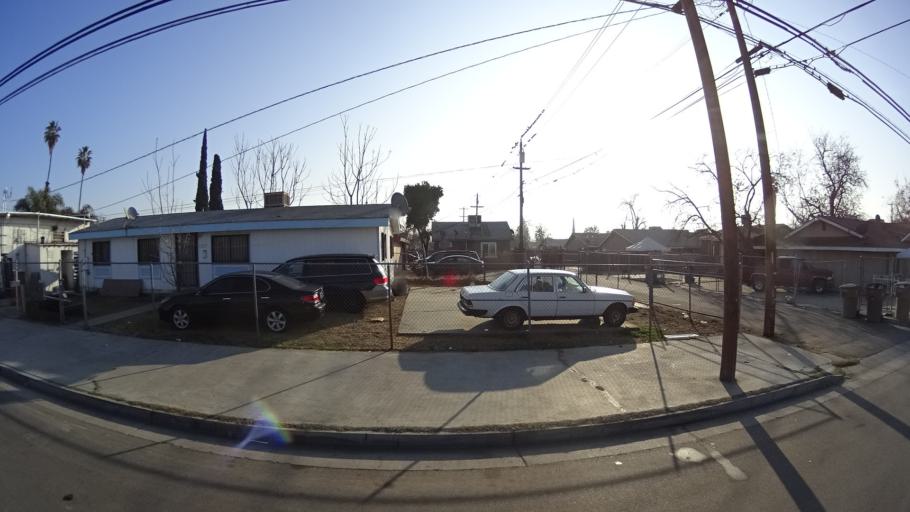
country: US
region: California
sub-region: Kern County
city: Bakersfield
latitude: 35.3801
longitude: -118.9850
